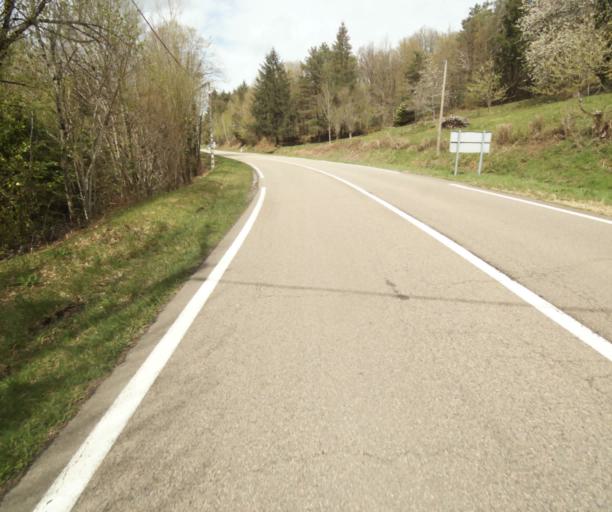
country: FR
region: Limousin
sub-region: Departement de la Correze
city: Sainte-Fortunade
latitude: 45.1979
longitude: 1.8346
